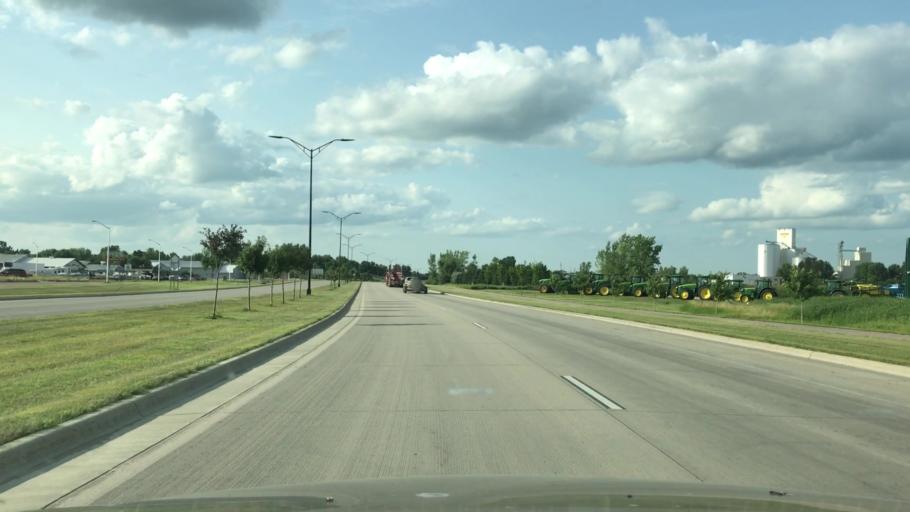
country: US
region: Minnesota
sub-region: Nobles County
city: Worthington
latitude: 43.6220
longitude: -95.5795
